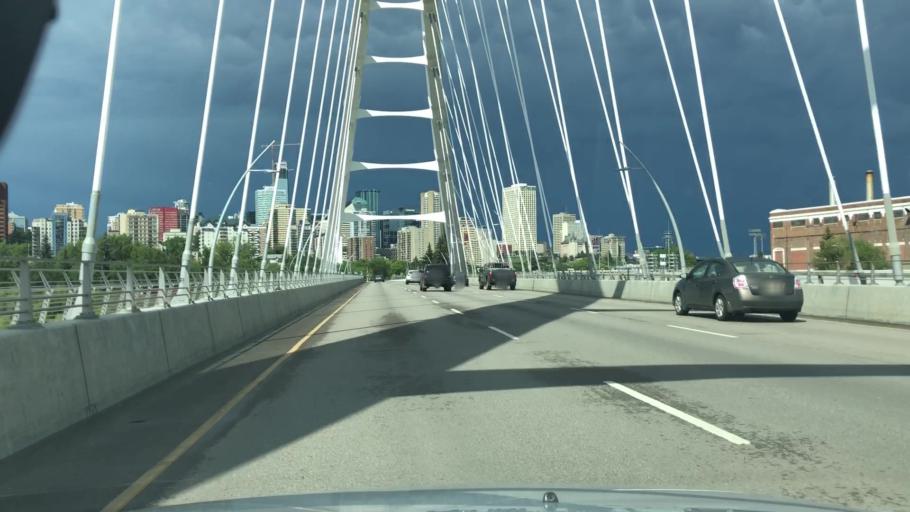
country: CA
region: Alberta
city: Edmonton
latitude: 53.5279
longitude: -113.5021
